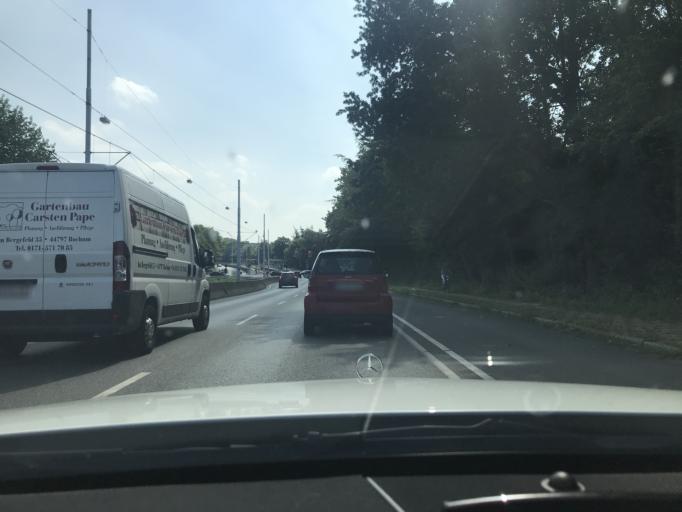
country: DE
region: North Rhine-Westphalia
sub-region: Regierungsbezirk Arnsberg
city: Bochum
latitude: 51.4588
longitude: 7.2369
